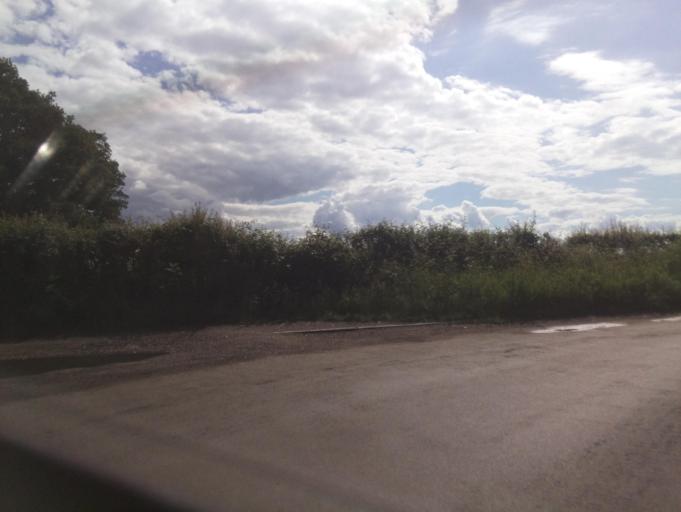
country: GB
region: England
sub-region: Hertfordshire
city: Chorleywood
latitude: 51.6544
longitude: -0.4648
